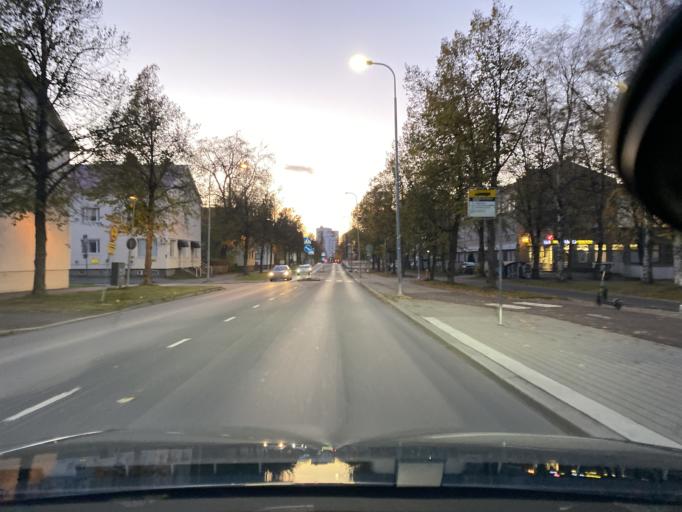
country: FI
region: Pirkanmaa
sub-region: Tampere
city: Tampere
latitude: 61.4706
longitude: 23.7330
